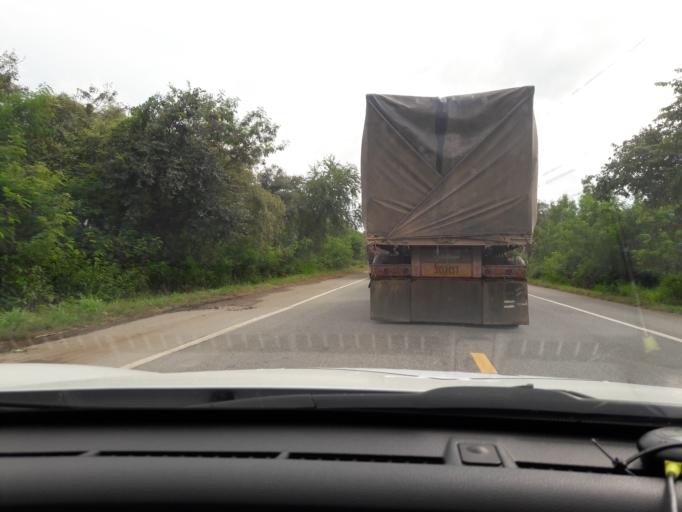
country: TH
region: Nakhon Sawan
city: Tak Fa
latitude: 15.4119
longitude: 100.5143
